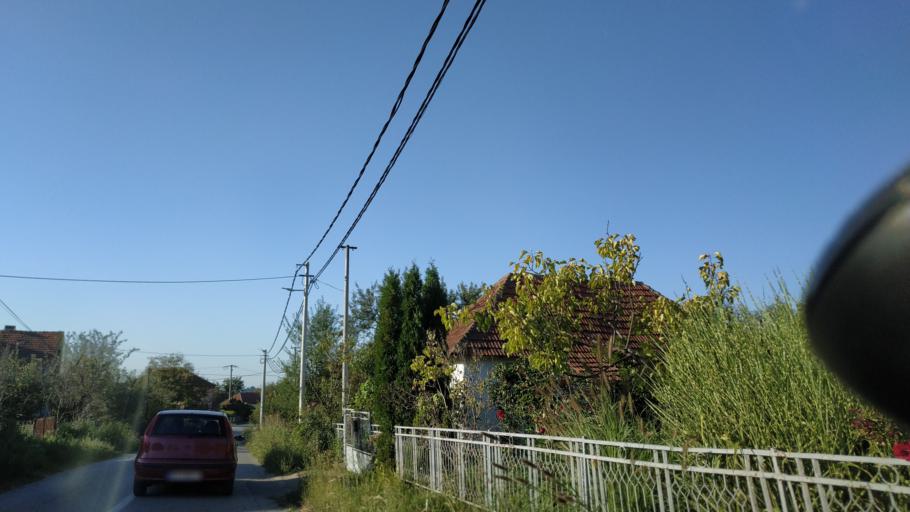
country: RS
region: Central Serbia
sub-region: Rasinski Okrug
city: Krusevac
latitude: 43.4940
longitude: 21.3426
